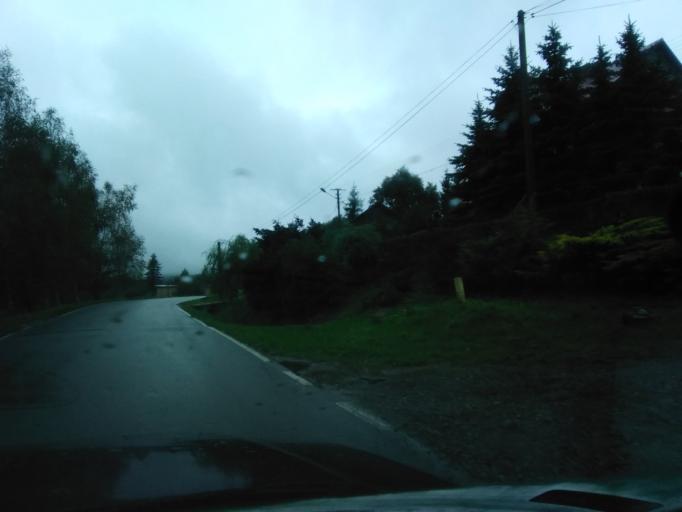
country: PL
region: Subcarpathian Voivodeship
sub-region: Powiat ropczycko-sedziszowski
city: Niedzwiada
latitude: 50.0347
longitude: 21.5457
